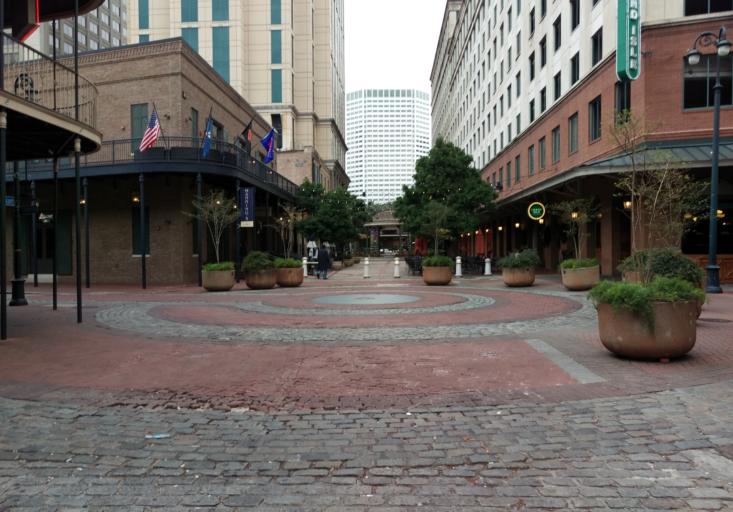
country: US
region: Louisiana
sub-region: Orleans Parish
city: New Orleans
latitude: 29.9469
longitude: -90.0654
